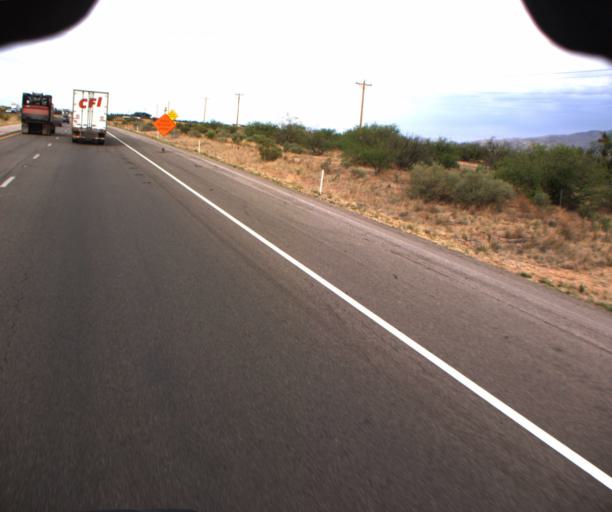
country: US
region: Arizona
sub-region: Cochise County
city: Whetstone
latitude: 31.9635
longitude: -110.3663
